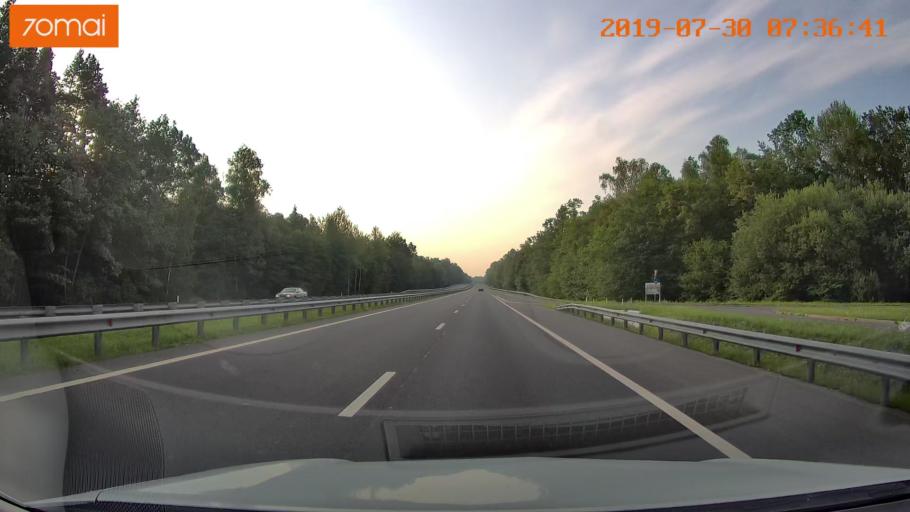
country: RU
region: Kaliningrad
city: Gvardeysk
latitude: 54.6622
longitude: 21.1301
